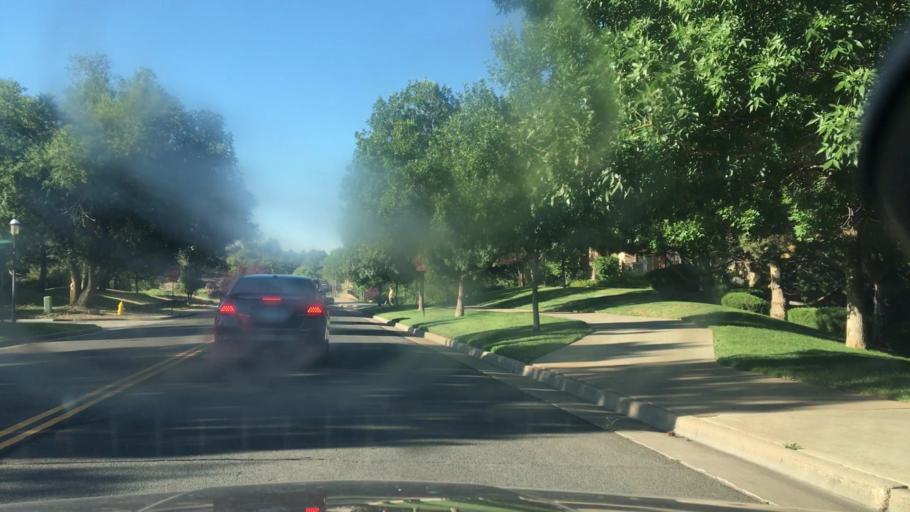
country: US
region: Colorado
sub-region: Arapahoe County
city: Castlewood
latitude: 39.6191
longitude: -104.8854
